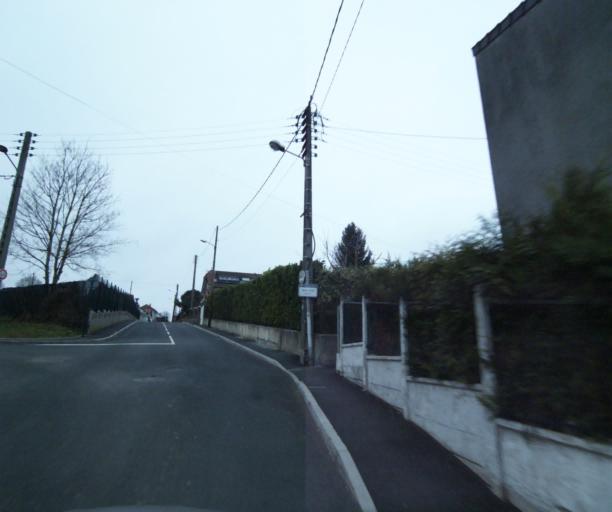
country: FR
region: Ile-de-France
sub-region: Departement du Val-de-Marne
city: Ablon-sur-Seine
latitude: 48.7266
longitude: 2.4144
